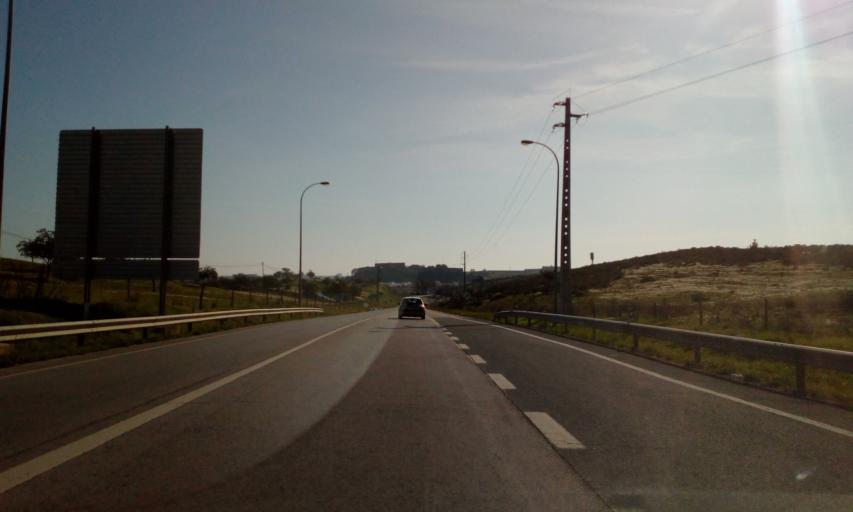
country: PT
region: Faro
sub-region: Castro Marim
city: Castro Marim
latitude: 37.2286
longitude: -7.4481
